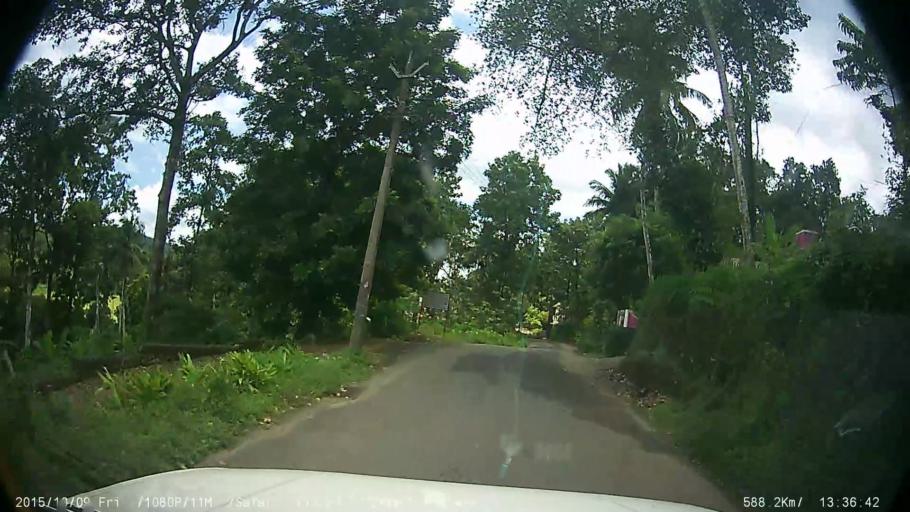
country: IN
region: Kerala
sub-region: Ernakulam
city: Piravam
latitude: 9.8974
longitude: 76.5621
